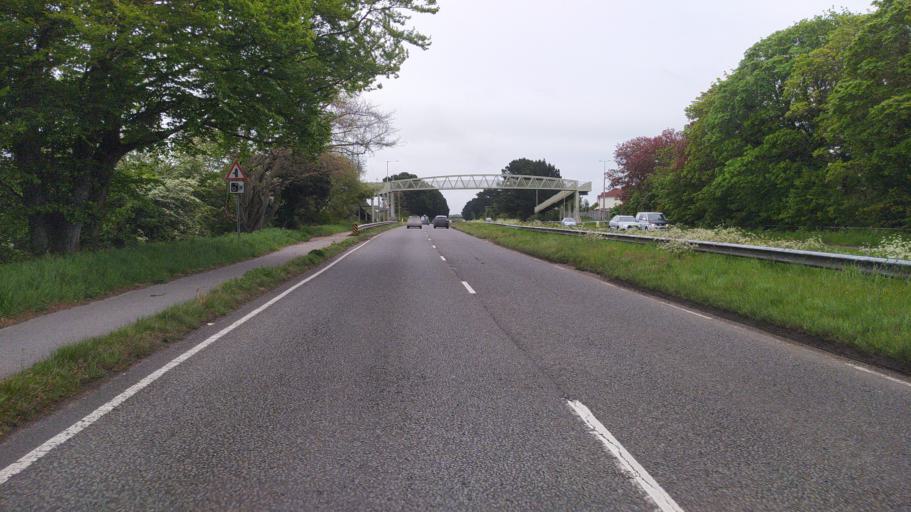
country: GB
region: England
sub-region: Dorset
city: Christchurch
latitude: 50.7430
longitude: -1.7598
